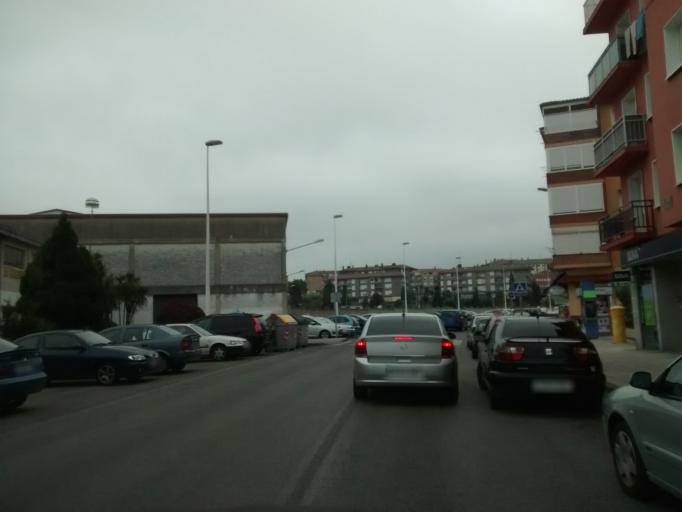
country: ES
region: Cantabria
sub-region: Provincia de Cantabria
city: Torrelavega
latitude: 43.3429
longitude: -4.0514
